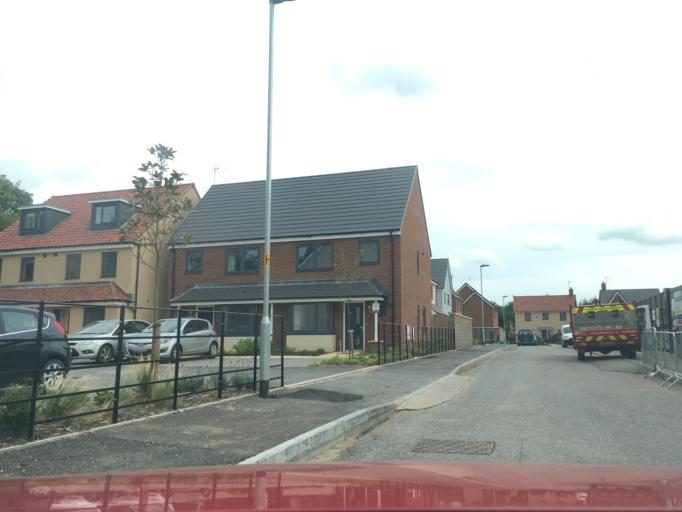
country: GB
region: England
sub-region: South Gloucestershire
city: Thornbury
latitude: 51.6022
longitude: -2.5158
